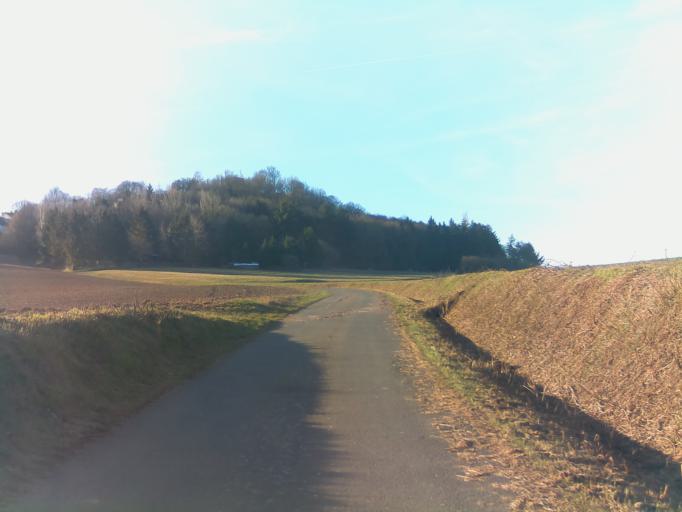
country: DE
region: Rheinland-Pfalz
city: Ruppertsecken
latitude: 49.6505
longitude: 7.8812
